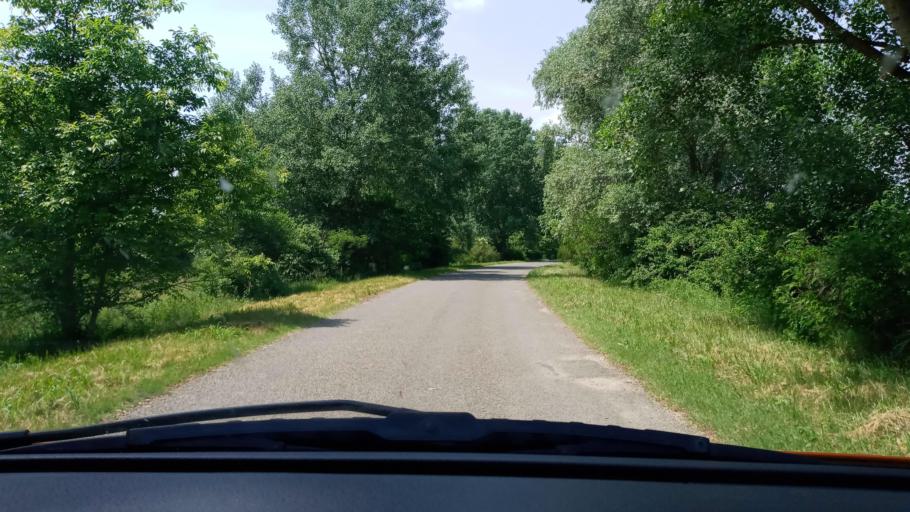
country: HU
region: Baranya
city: Sellye
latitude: 45.8061
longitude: 17.8832
